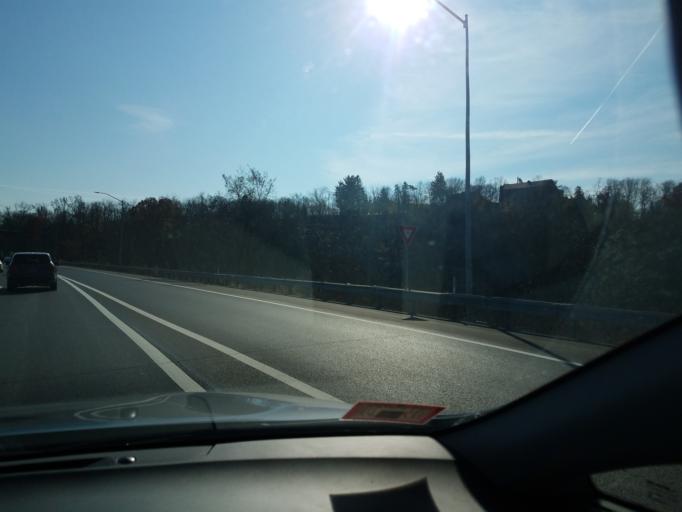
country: US
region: Pennsylvania
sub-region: Allegheny County
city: Bellevue
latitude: 40.5107
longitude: -80.0495
